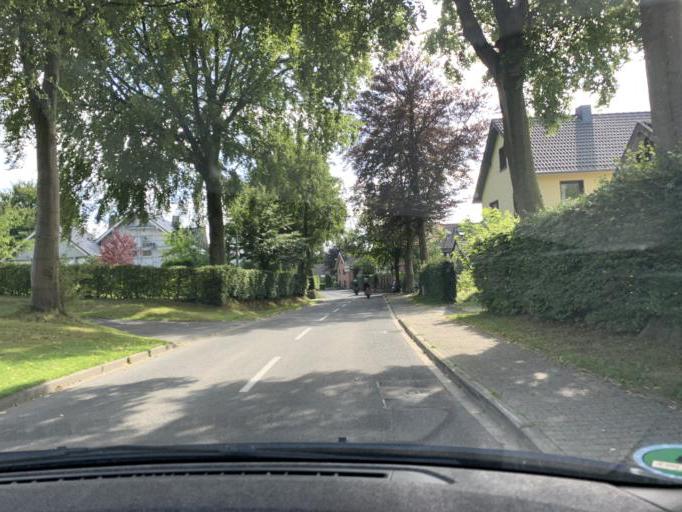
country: DE
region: North Rhine-Westphalia
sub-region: Regierungsbezirk Koln
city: Monschau
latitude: 50.5920
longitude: 6.2558
